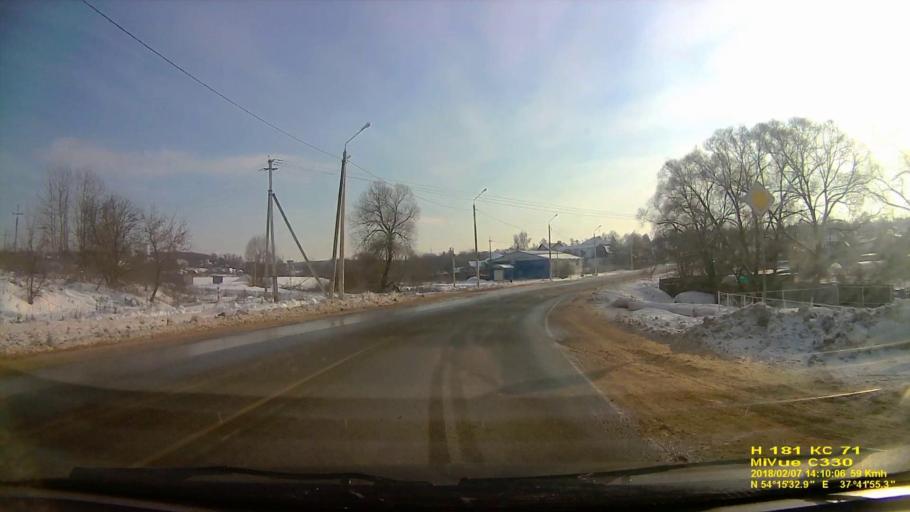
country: RU
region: Tula
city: Gorelki
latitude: 54.2593
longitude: 37.6988
